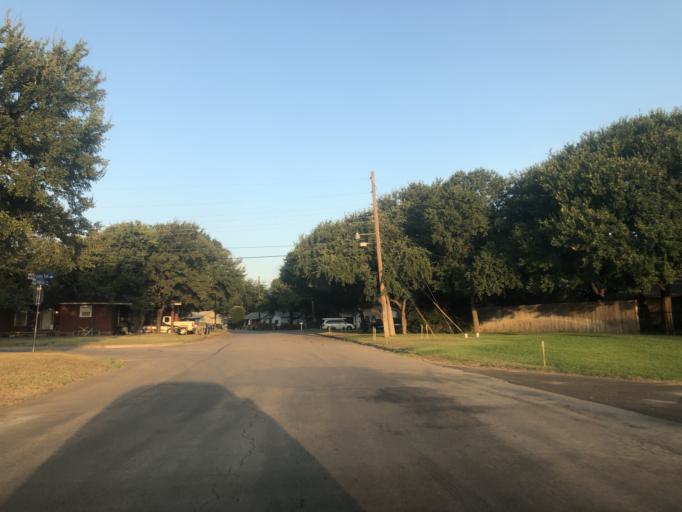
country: US
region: Texas
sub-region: Tarrant County
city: Lake Worth
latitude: 32.8078
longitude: -97.4465
